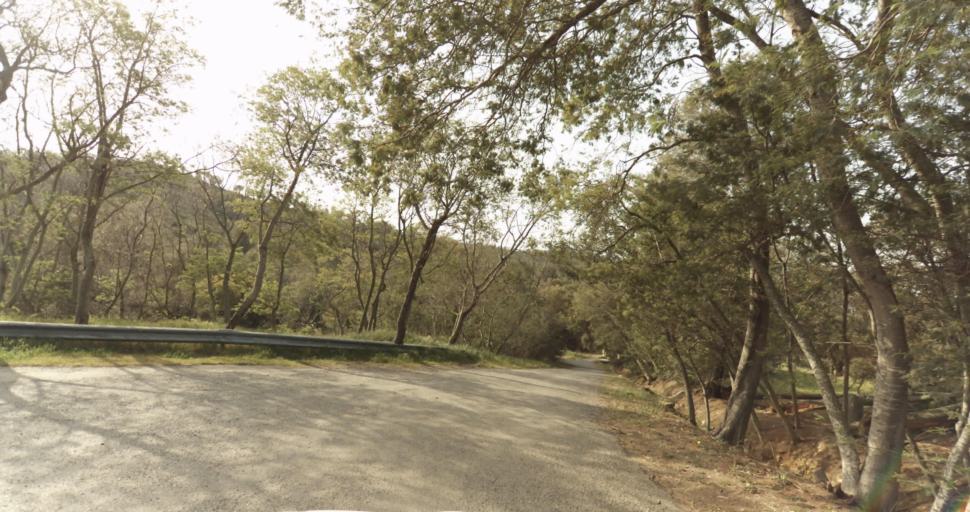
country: FR
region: Provence-Alpes-Cote d'Azur
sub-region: Departement du Var
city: Bormes-les-Mimosas
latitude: 43.1399
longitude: 6.2893
